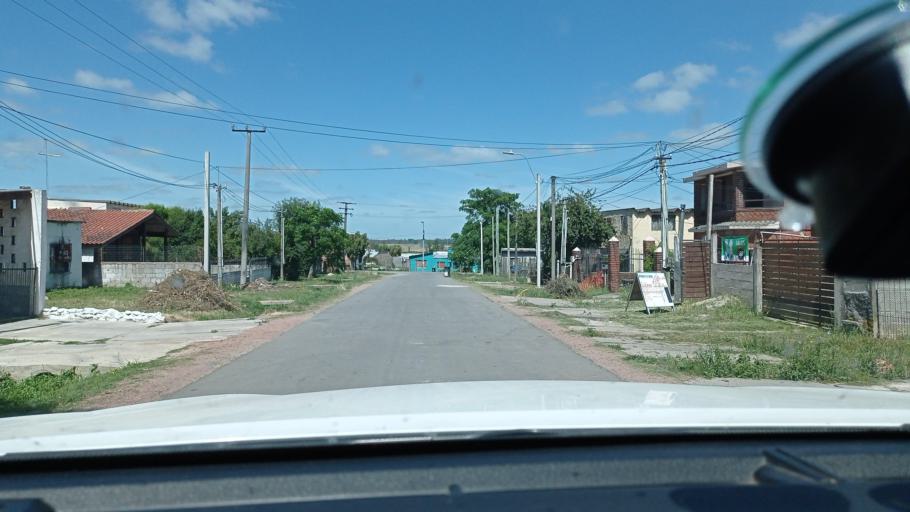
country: UY
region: Canelones
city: Pando
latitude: -34.7162
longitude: -55.9686
